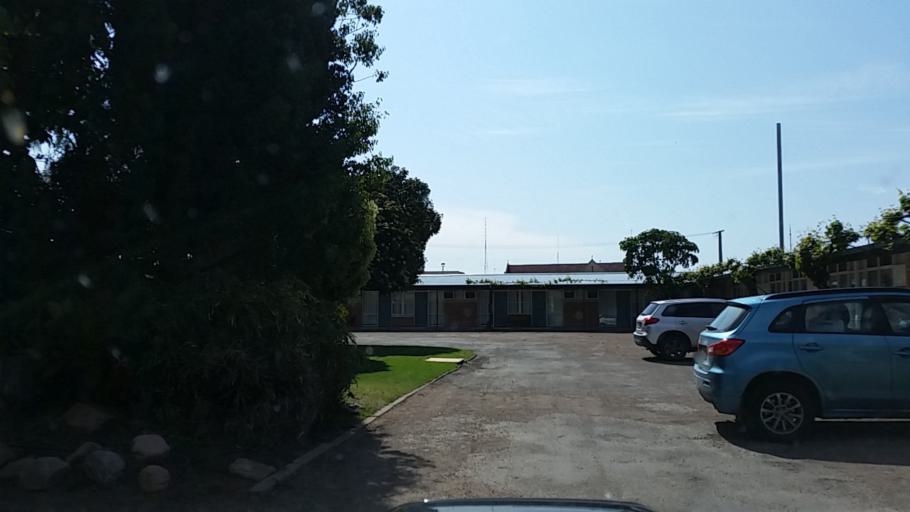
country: AU
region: South Australia
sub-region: Port Pirie City and Dists
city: Port Pirie
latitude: -33.1812
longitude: 138.0093
